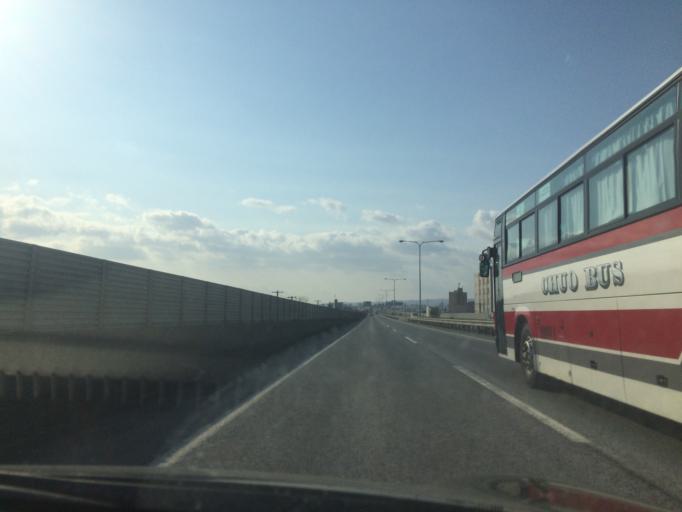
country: JP
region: Hokkaido
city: Sapporo
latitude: 43.0687
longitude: 141.4227
